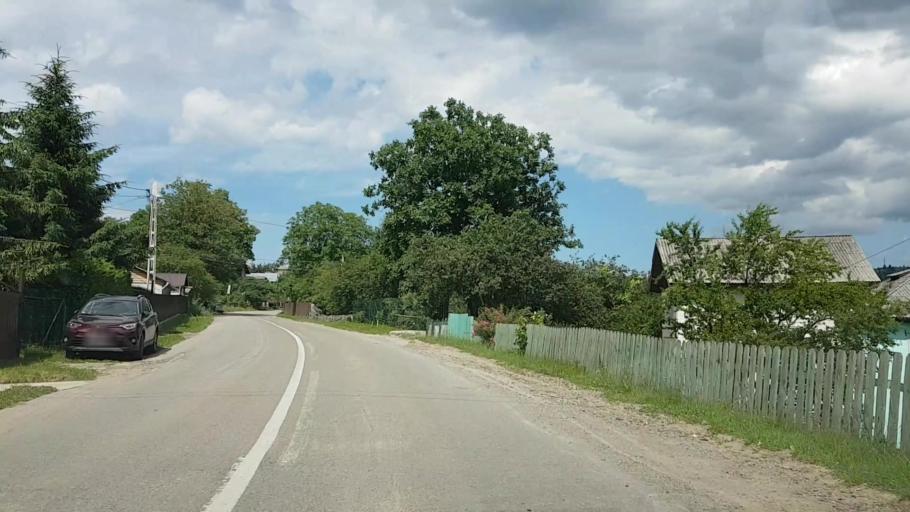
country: RO
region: Neamt
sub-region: Comuna Hangu
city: Hangu
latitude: 47.0483
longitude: 26.0188
